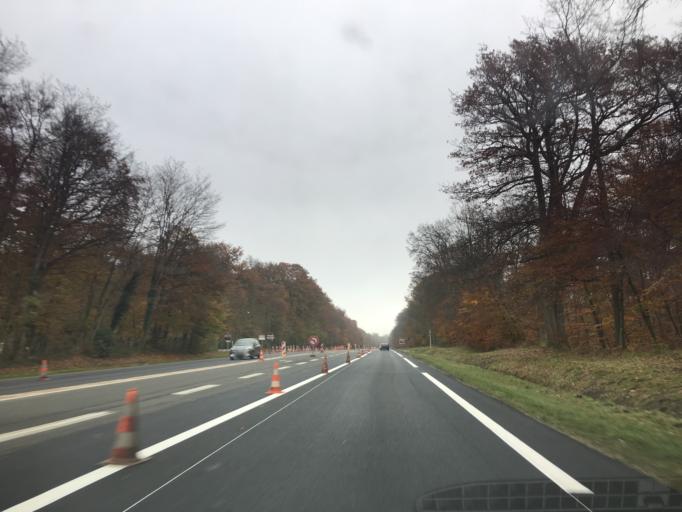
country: FR
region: Ile-de-France
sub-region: Departement de Seine-et-Marne
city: Avon
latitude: 48.3961
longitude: 2.7252
